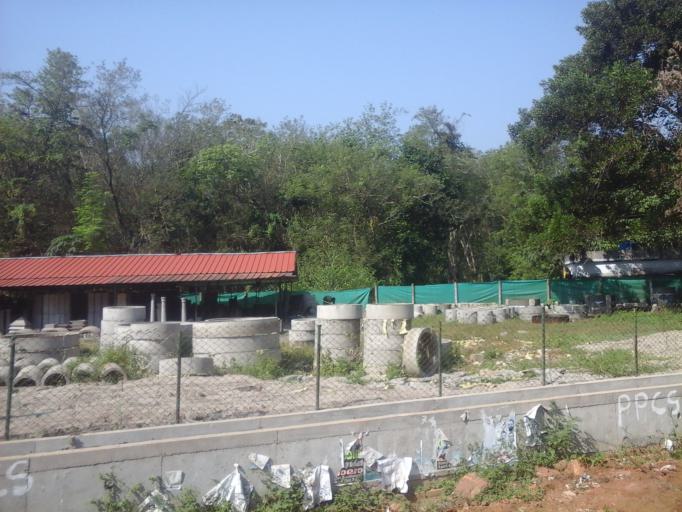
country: IN
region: Kerala
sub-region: Kottayam
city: Lalam
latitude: 9.6867
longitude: 76.6936
